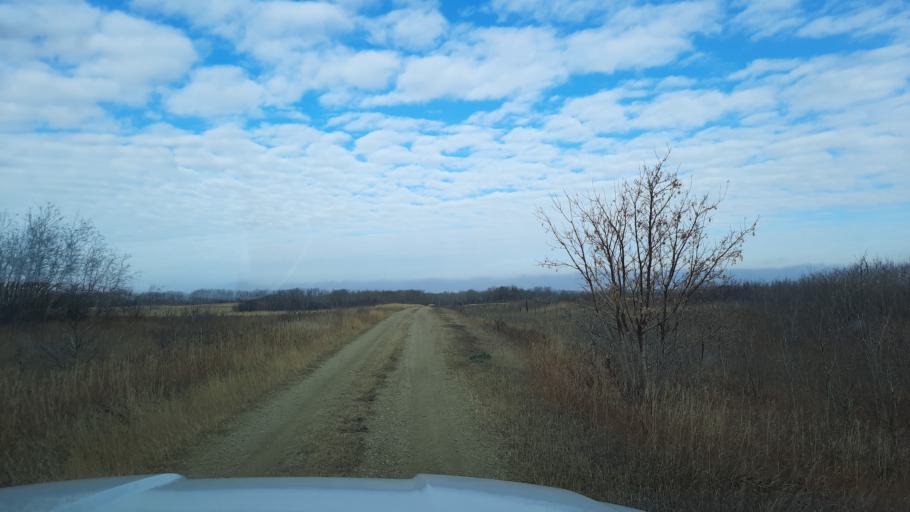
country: CA
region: Saskatchewan
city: Pilot Butte
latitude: 50.7718
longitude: -104.2153
